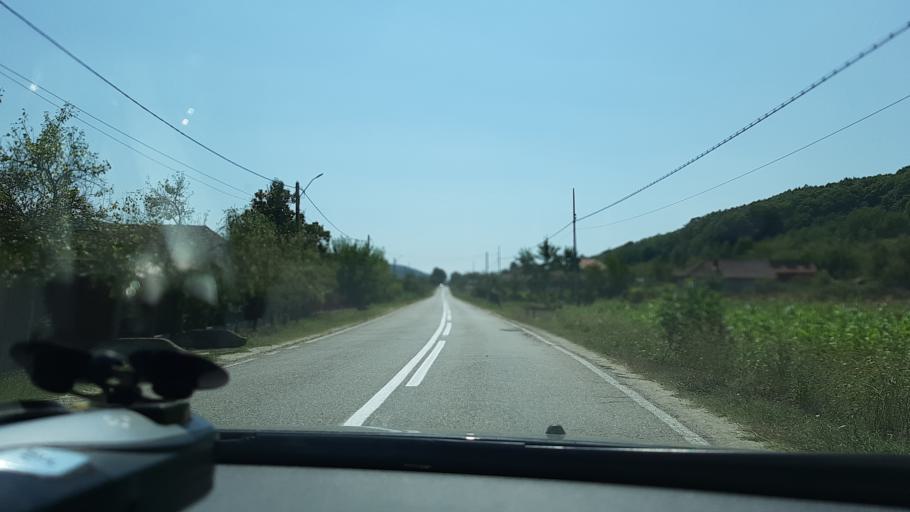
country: RO
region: Gorj
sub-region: Comuna Licuriciu
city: Licuriciu
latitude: 44.8754
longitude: 23.6312
